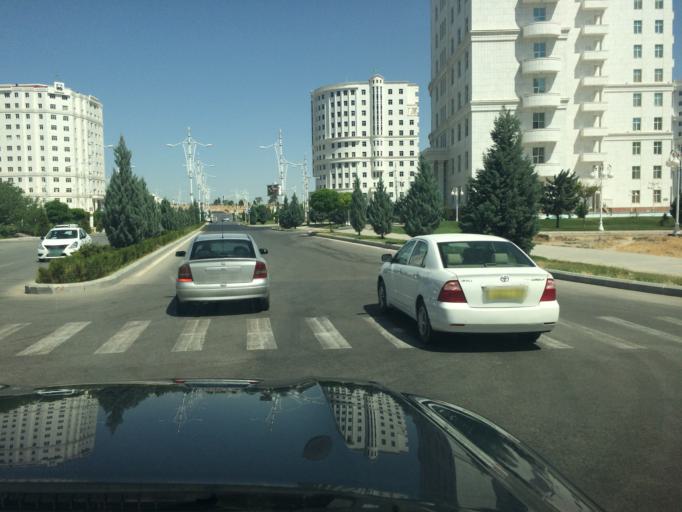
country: TM
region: Ahal
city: Ashgabat
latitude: 37.9198
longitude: 58.3606
